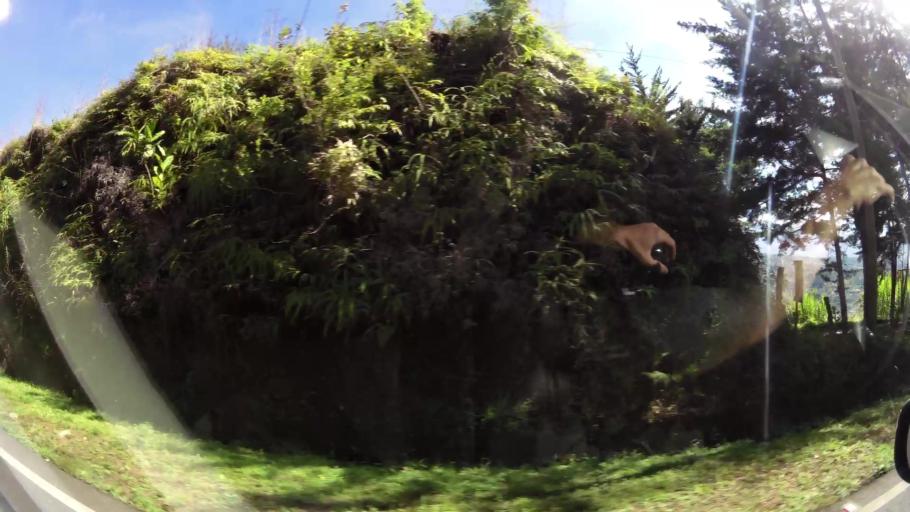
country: CR
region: San Jose
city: San Isidro
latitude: 9.4237
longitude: -83.7118
